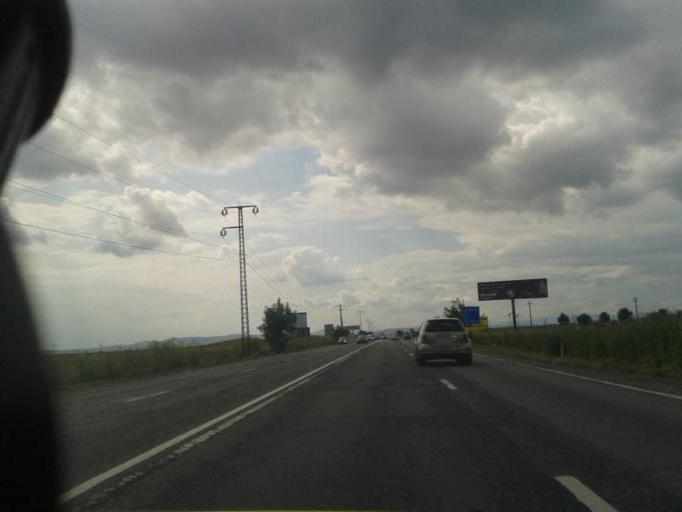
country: RO
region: Prahova
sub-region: Oras Baicoi
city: Liliesti
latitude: 45.0019
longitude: 25.8861
